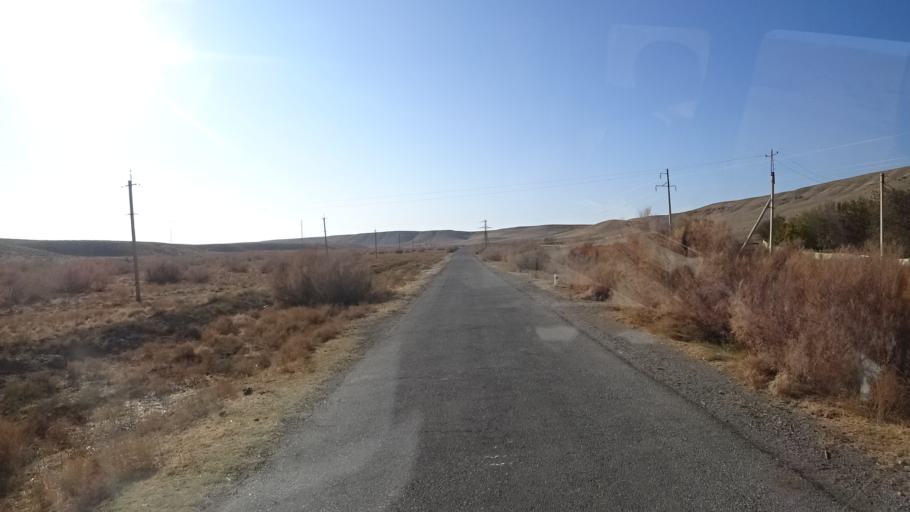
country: UZ
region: Navoiy
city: Beshrabot
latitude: 40.2574
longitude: 65.4498
